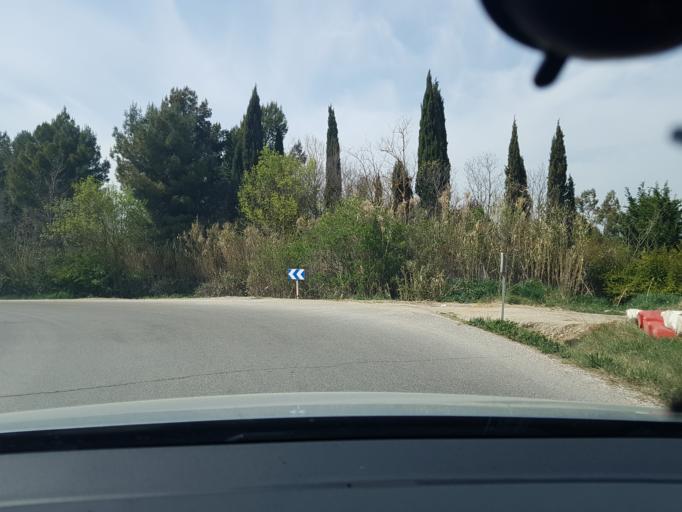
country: FR
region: Provence-Alpes-Cote d'Azur
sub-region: Departement des Bouches-du-Rhone
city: Bouc-Bel-Air
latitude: 43.4736
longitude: 5.3974
